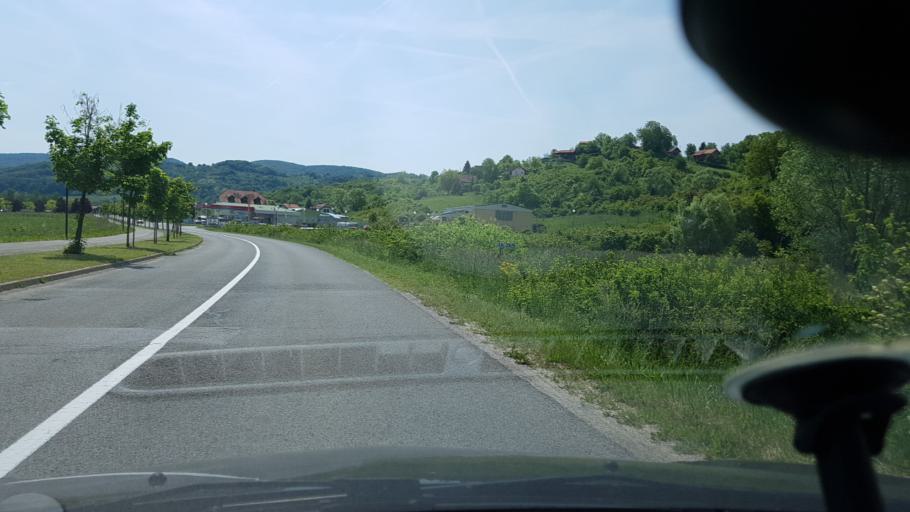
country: HR
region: Krapinsko-Zagorska
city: Marija Bistrica
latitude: 46.0033
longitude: 16.1115
